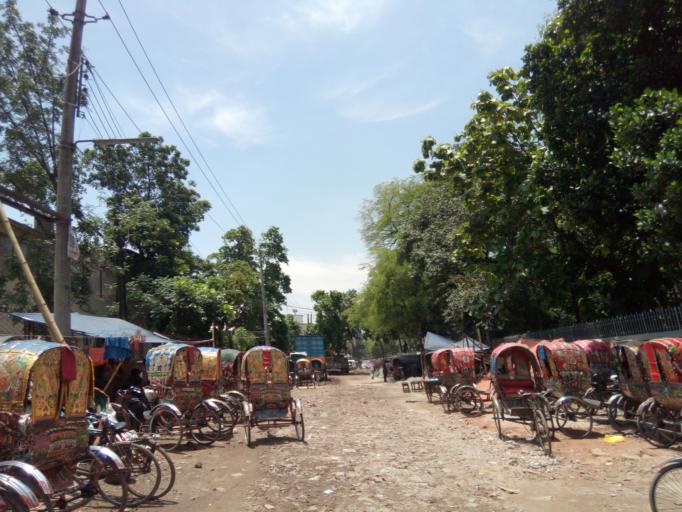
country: BD
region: Dhaka
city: Paltan
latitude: 23.7654
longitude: 90.3989
